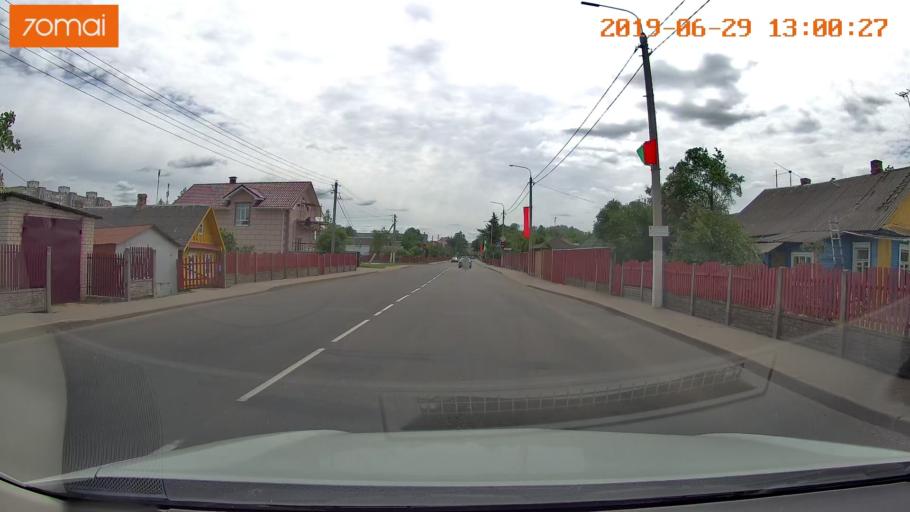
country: BY
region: Minsk
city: Slutsk
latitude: 53.0445
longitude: 27.5571
